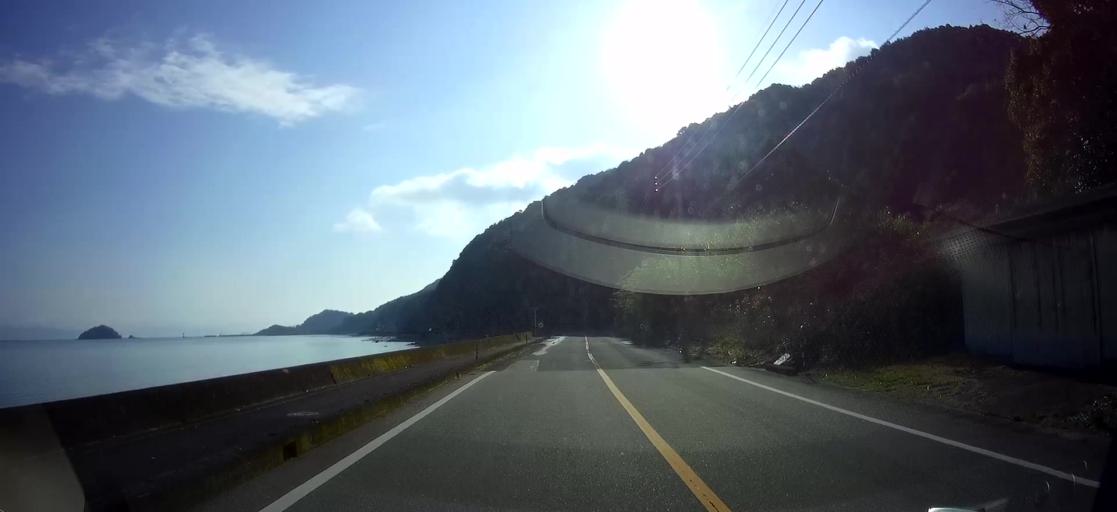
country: JP
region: Kumamoto
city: Yatsushiro
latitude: 32.4870
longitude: 130.4380
